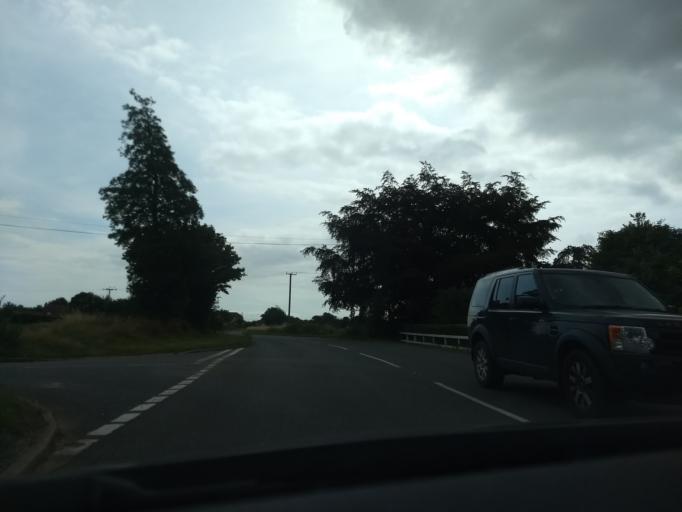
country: GB
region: England
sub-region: Suffolk
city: Shotley Gate
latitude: 51.9910
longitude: 1.1993
